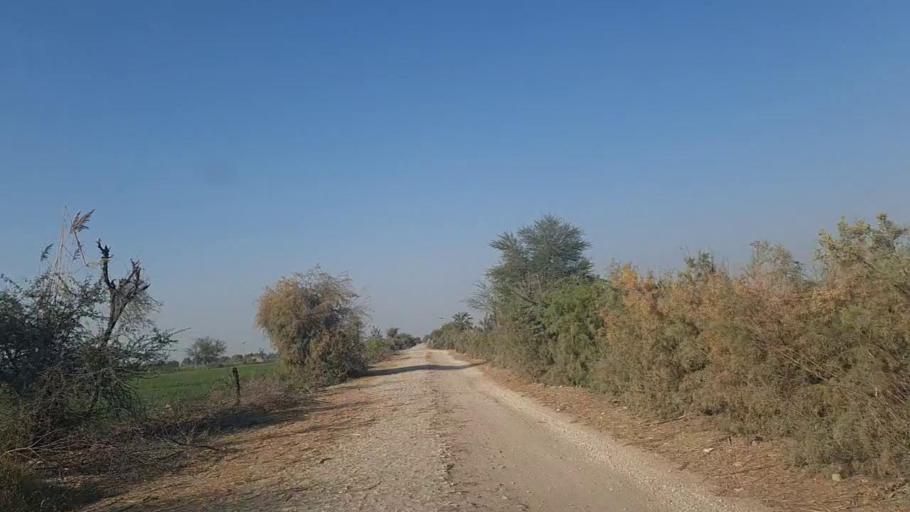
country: PK
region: Sindh
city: Jam Sahib
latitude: 26.3168
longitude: 68.7148
